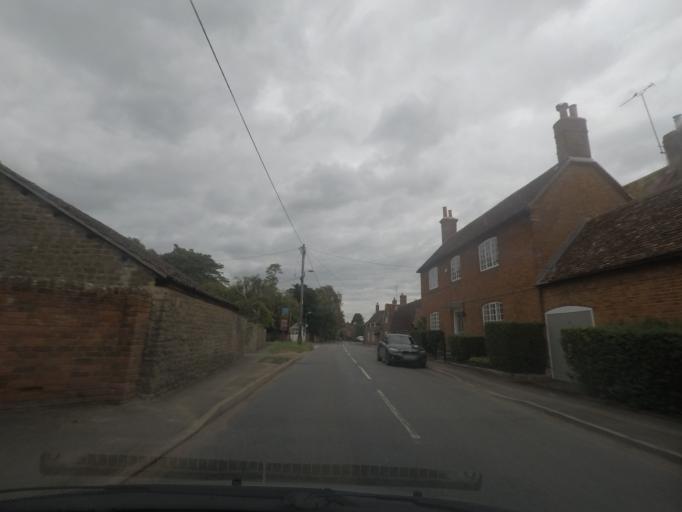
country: GB
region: England
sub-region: Oxfordshire
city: Sutton Courtenay
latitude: 51.6274
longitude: -1.2994
